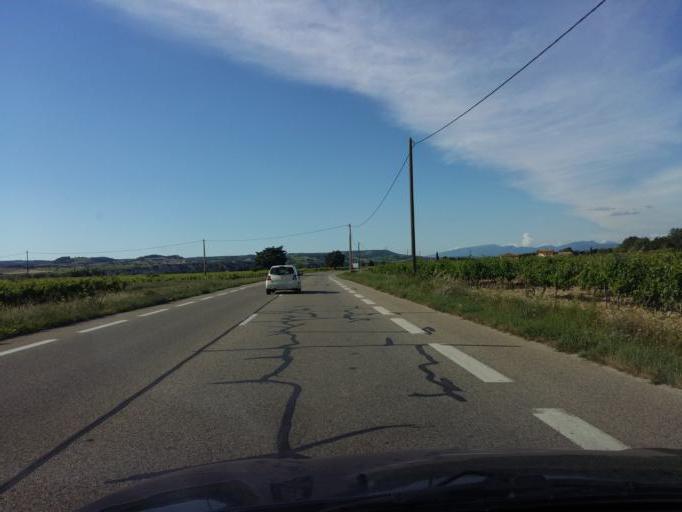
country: FR
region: Provence-Alpes-Cote d'Azur
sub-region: Departement du Vaucluse
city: Sablet
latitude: 44.1997
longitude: 4.9992
